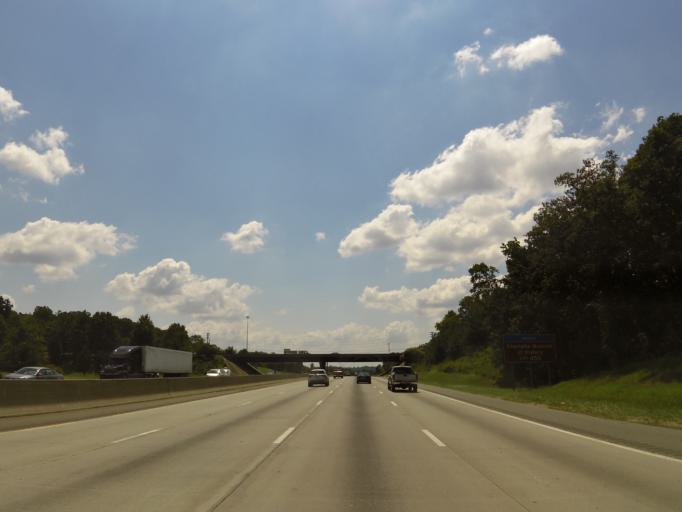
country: US
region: North Carolina
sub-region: Cabarrus County
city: Harrisburg
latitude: 35.3339
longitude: -80.7438
